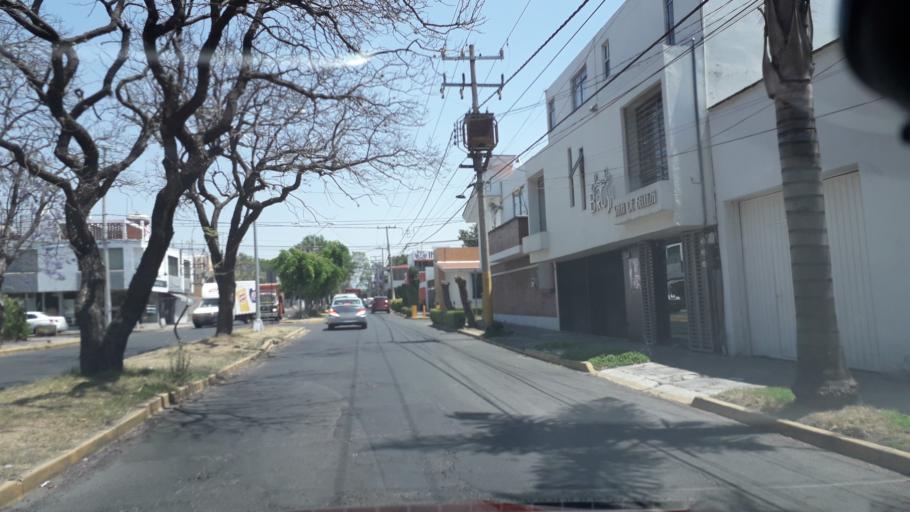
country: MX
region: Puebla
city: Puebla
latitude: 19.0246
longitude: -98.1930
